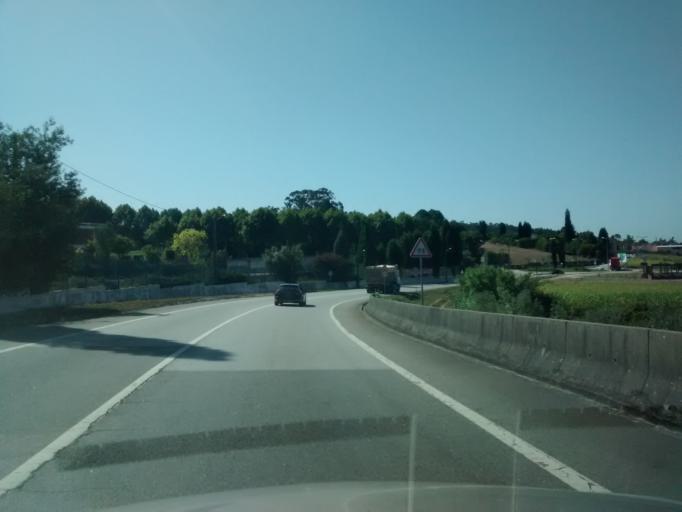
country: PT
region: Aveiro
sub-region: Anadia
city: Arcos
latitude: 40.4397
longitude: -8.4522
